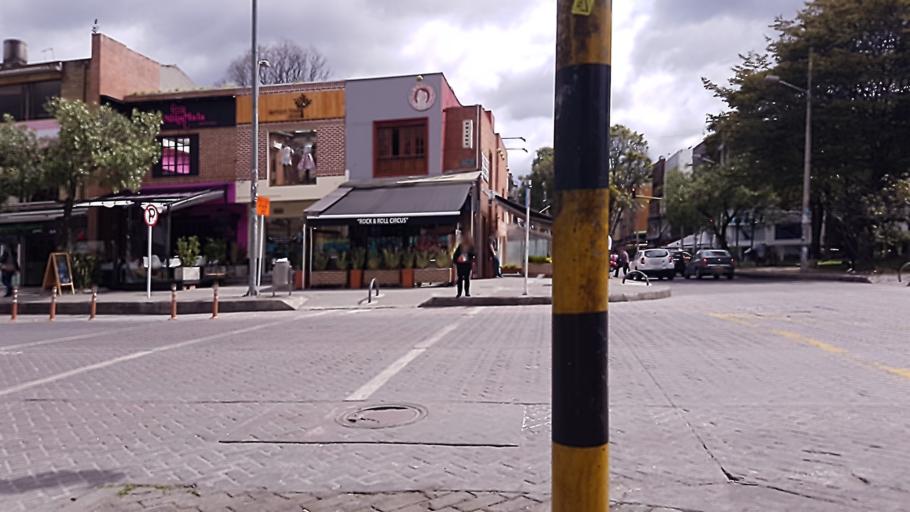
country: CO
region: Bogota D.C.
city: Barrio San Luis
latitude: 4.6692
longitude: -74.0536
